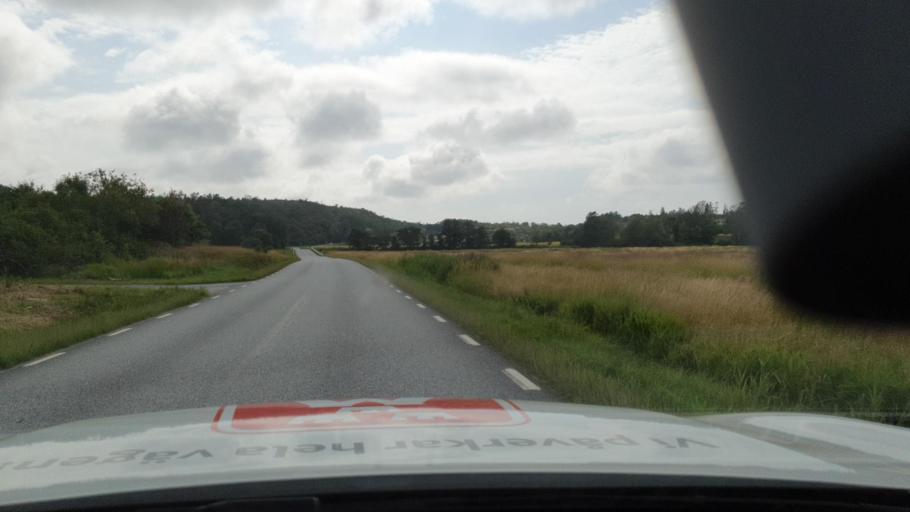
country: SE
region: Vaestra Goetaland
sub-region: Sotenas Kommun
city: Hunnebostrand
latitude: 58.5726
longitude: 11.3157
